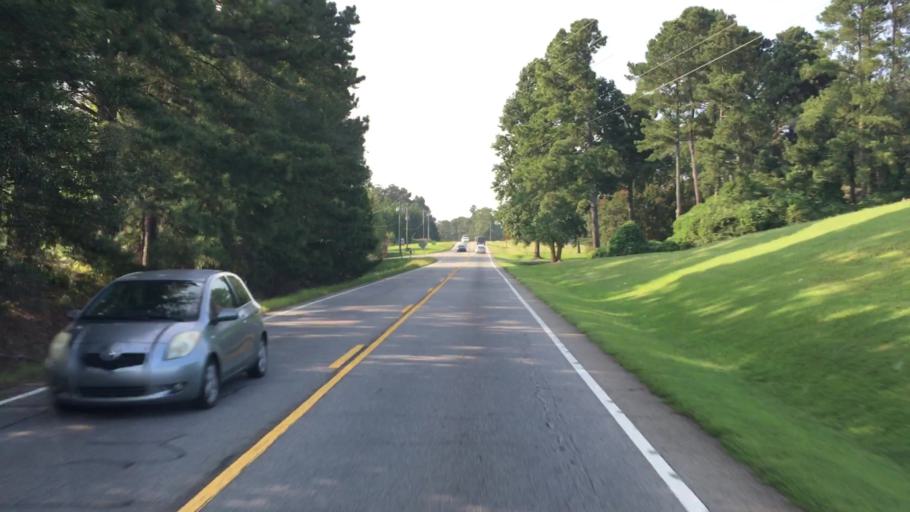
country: US
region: Georgia
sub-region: Jackson County
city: Braselton
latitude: 34.1478
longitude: -83.7981
